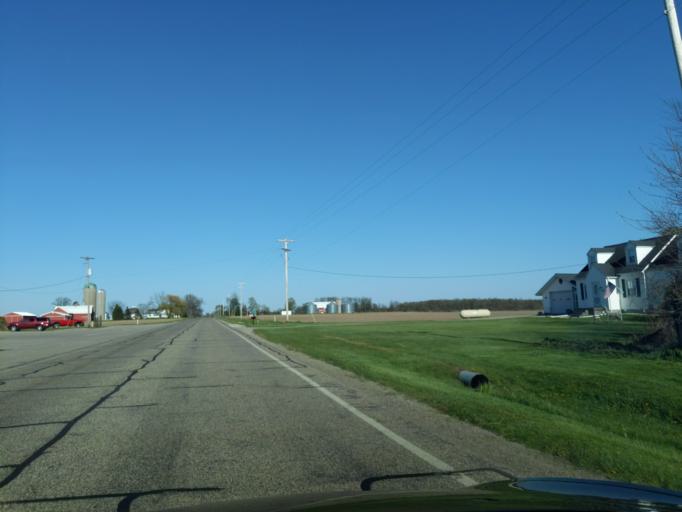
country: US
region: Michigan
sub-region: Ionia County
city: Ionia
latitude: 42.8858
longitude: -85.0223
